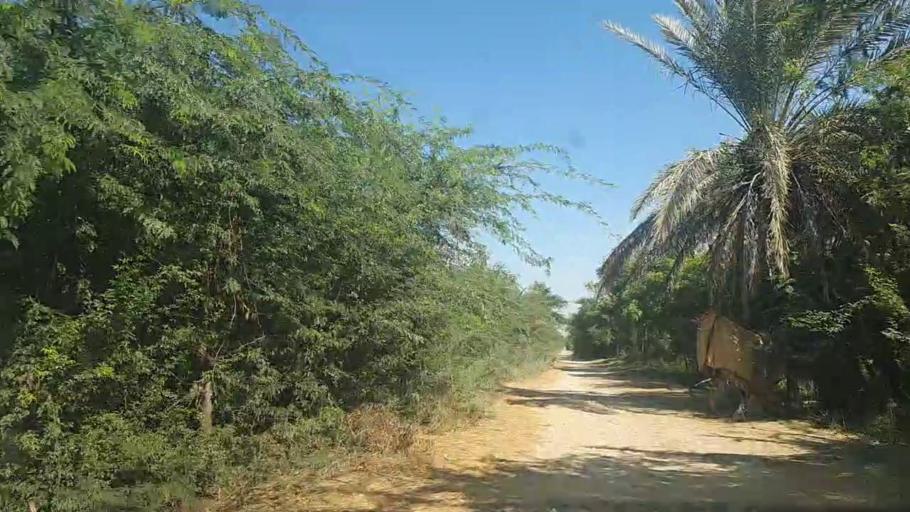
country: PK
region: Sindh
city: Mirpur Batoro
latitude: 24.7009
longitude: 68.2370
